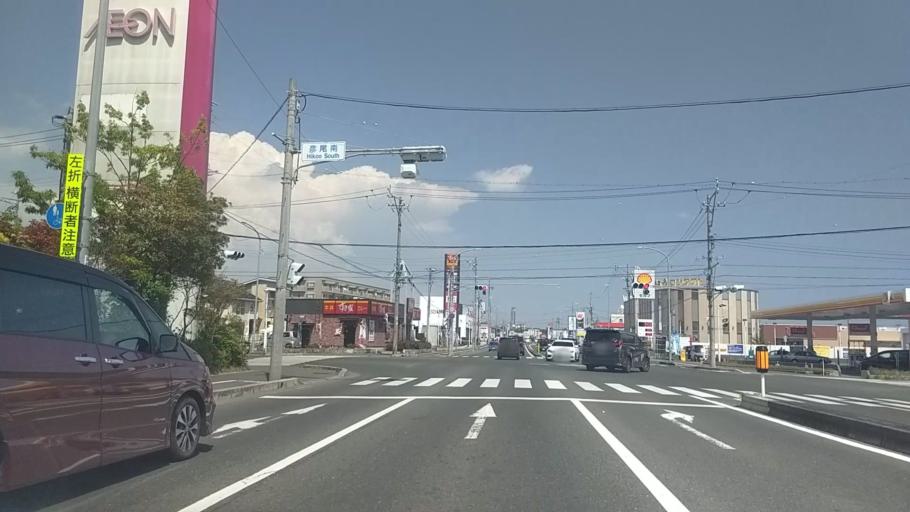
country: JP
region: Shizuoka
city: Hamamatsu
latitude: 34.6986
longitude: 137.6906
